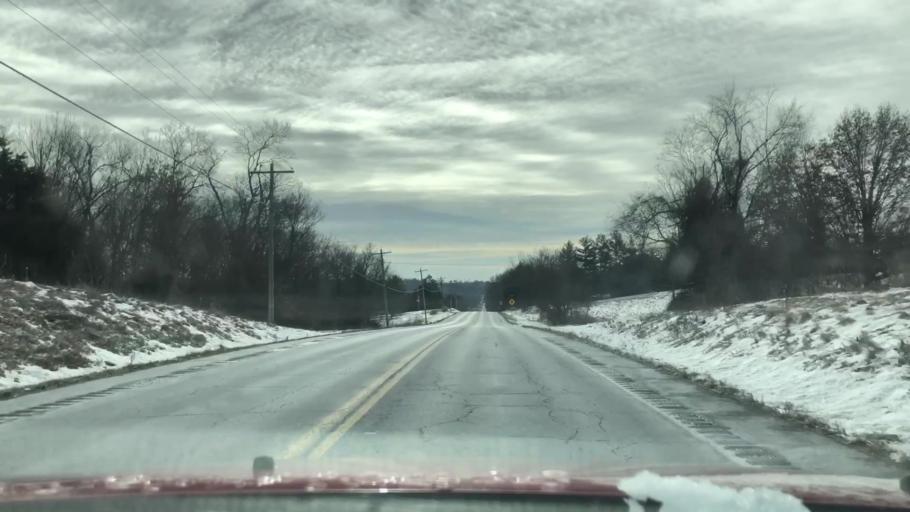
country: US
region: Missouri
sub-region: Jackson County
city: Oak Grove
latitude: 38.9642
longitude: -94.1311
